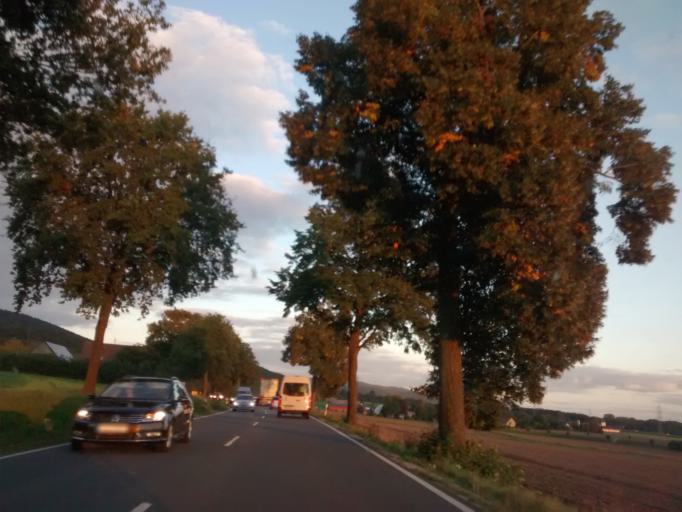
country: DE
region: North Rhine-Westphalia
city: Borgholzhausen
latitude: 52.0759
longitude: 8.3206
